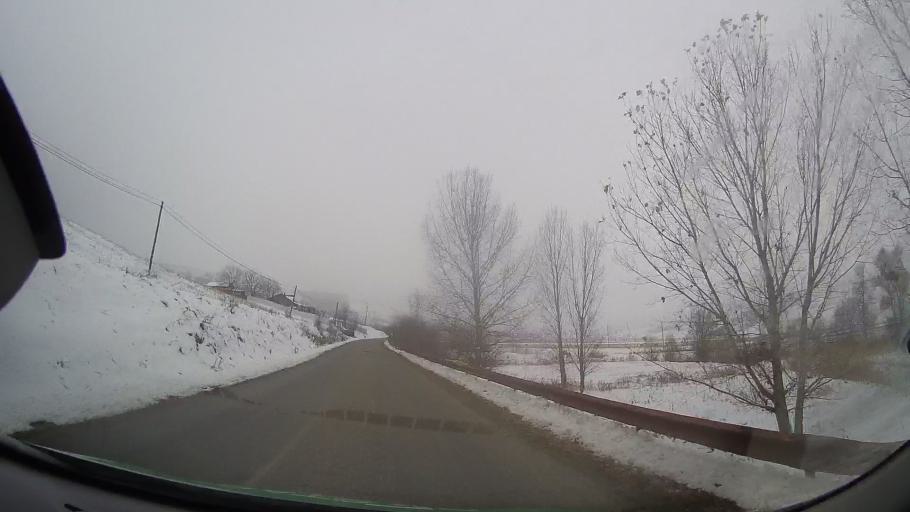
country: RO
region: Bacau
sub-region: Comuna Vultureni
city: Vultureni
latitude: 46.3957
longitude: 27.2775
